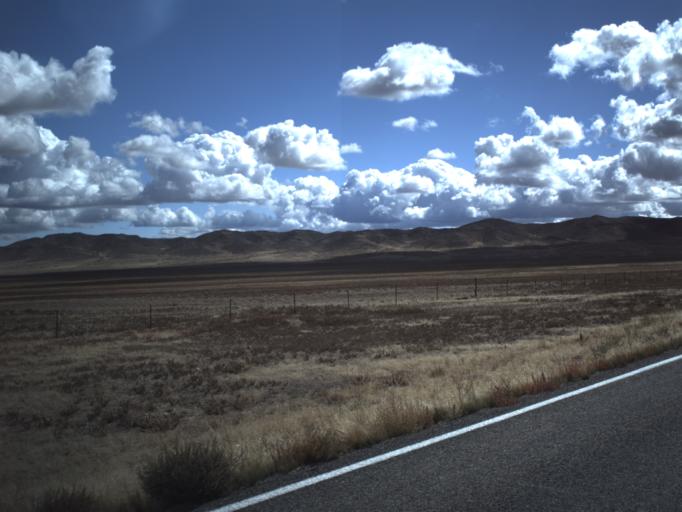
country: US
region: Utah
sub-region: Beaver County
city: Milford
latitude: 38.6686
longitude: -113.8831
